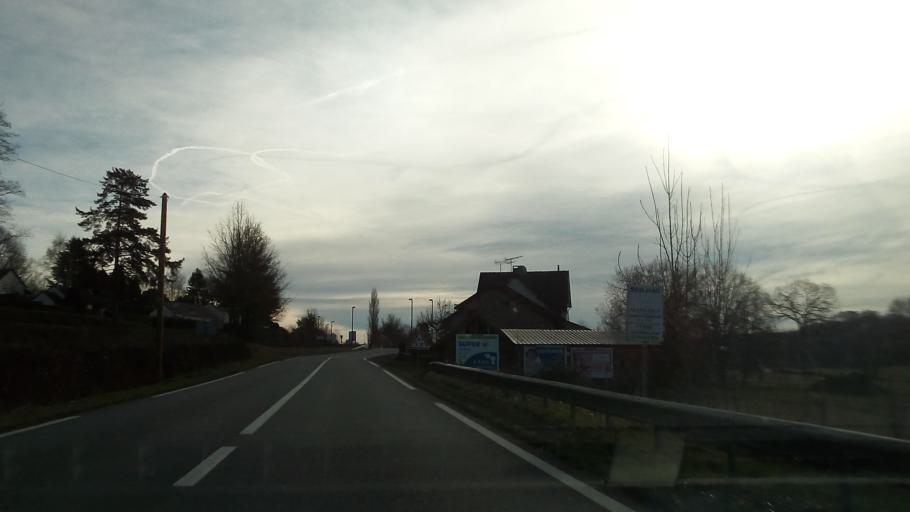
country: FR
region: Limousin
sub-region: Departement de la Correze
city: Seilhac
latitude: 45.3736
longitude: 1.6951
